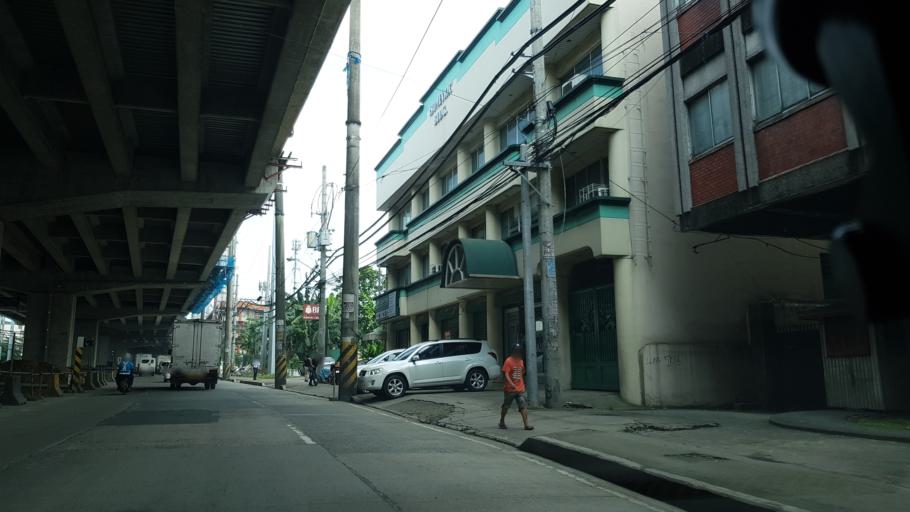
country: PH
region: Metro Manila
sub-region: San Juan
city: San Juan
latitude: 14.6161
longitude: 121.0166
